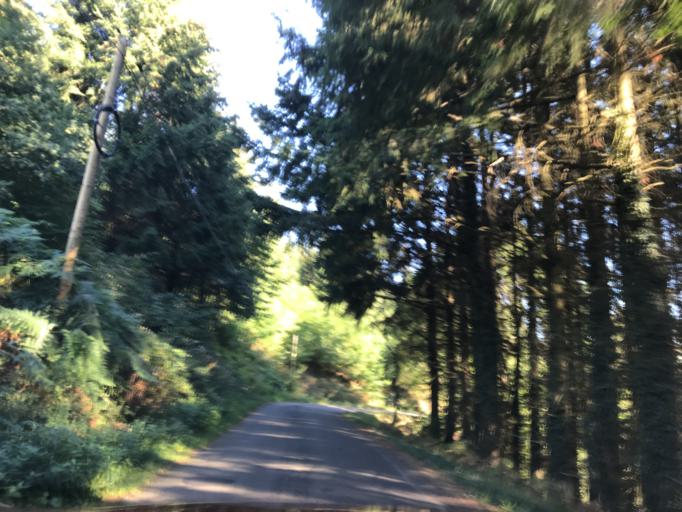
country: FR
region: Auvergne
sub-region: Departement du Puy-de-Dome
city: Escoutoux
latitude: 45.7779
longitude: 3.6074
